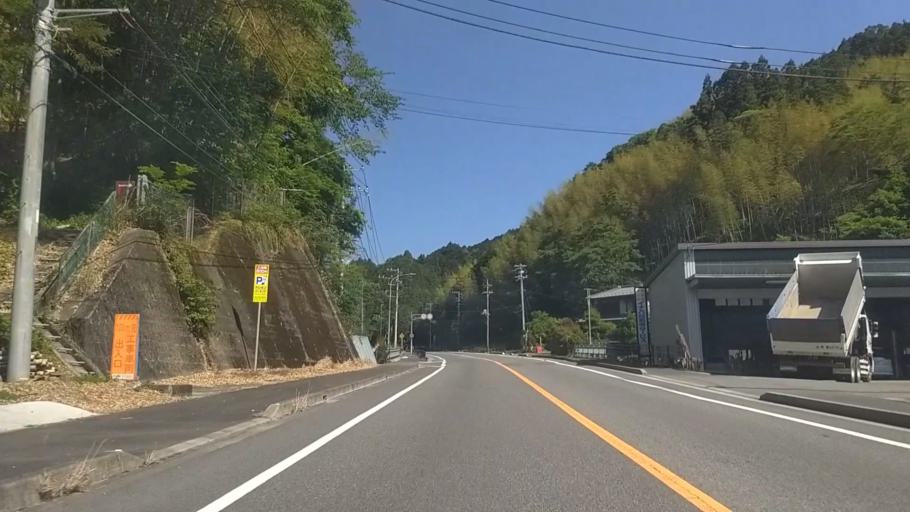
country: JP
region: Shizuoka
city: Fujinomiya
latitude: 35.2658
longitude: 138.4614
